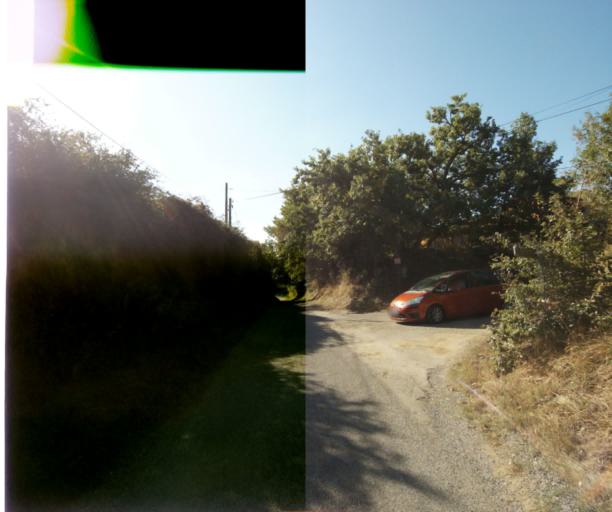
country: FR
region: Midi-Pyrenees
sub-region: Departement du Tarn-et-Garonne
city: Verdun-sur-Garonne
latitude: 43.8608
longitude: 1.2262
